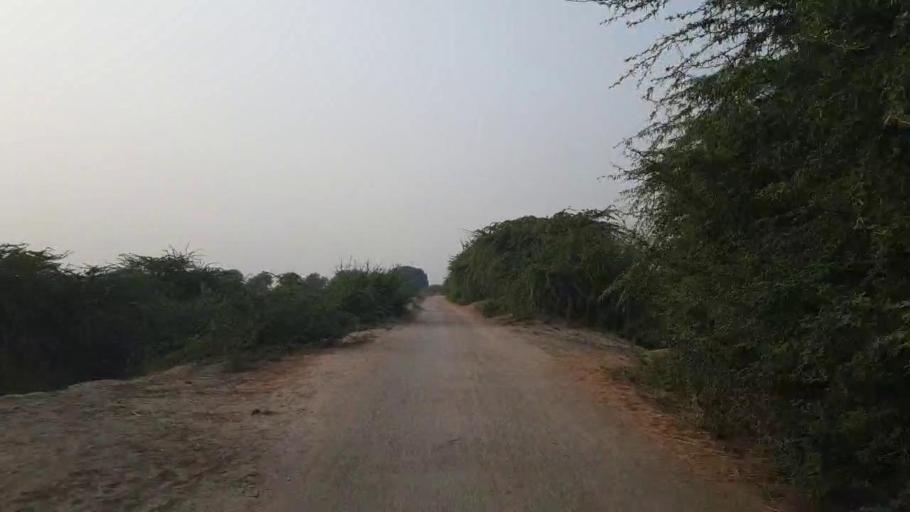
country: PK
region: Sindh
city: Mirpur Batoro
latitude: 24.6502
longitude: 68.3896
